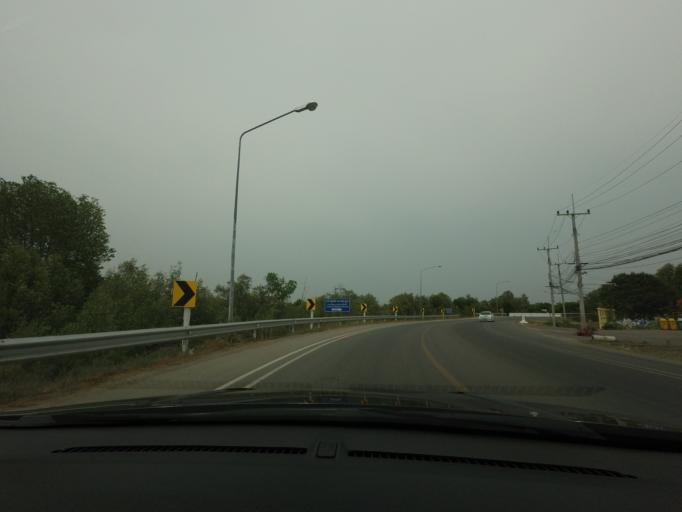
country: TH
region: Phetchaburi
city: Ban Laem
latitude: 13.2725
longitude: 99.9356
